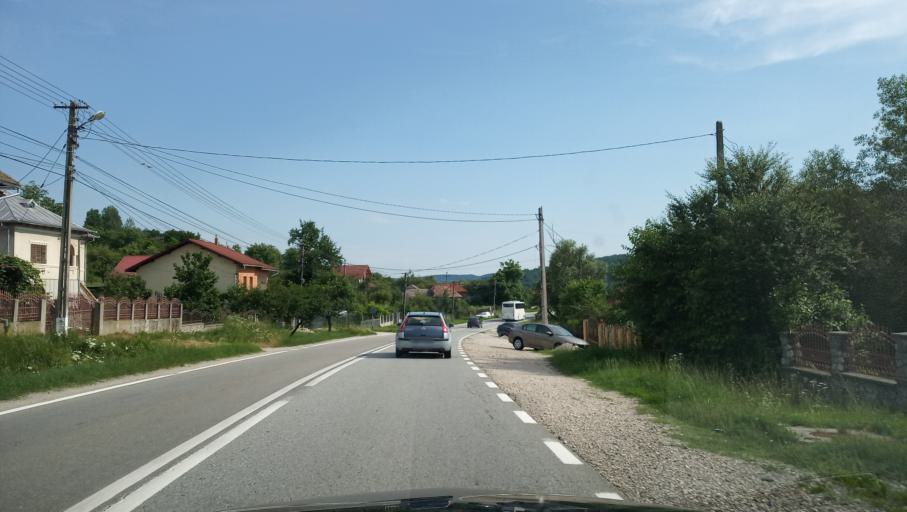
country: RO
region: Valcea
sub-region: Comuna Pietrari
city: Pietrarii de Sus
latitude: 45.1170
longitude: 24.1161
